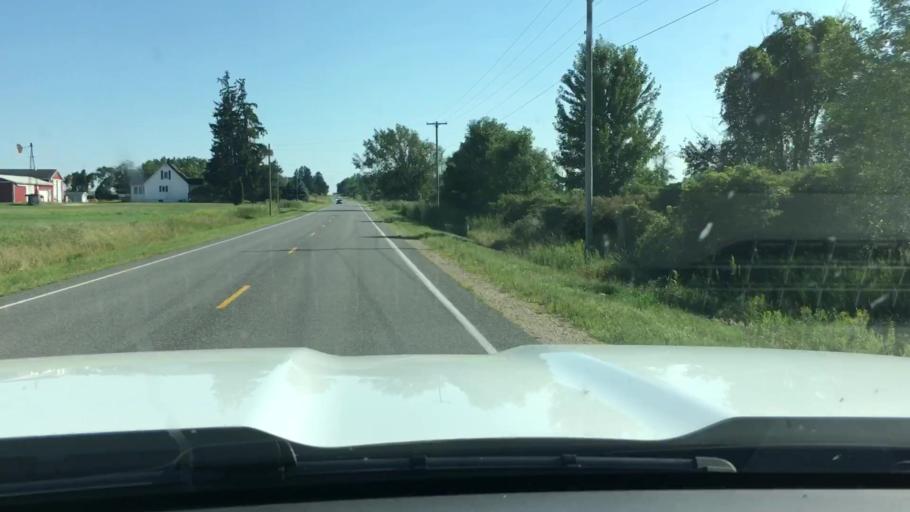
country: US
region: Michigan
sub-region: Muskegon County
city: Ravenna
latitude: 43.1726
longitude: -85.9279
